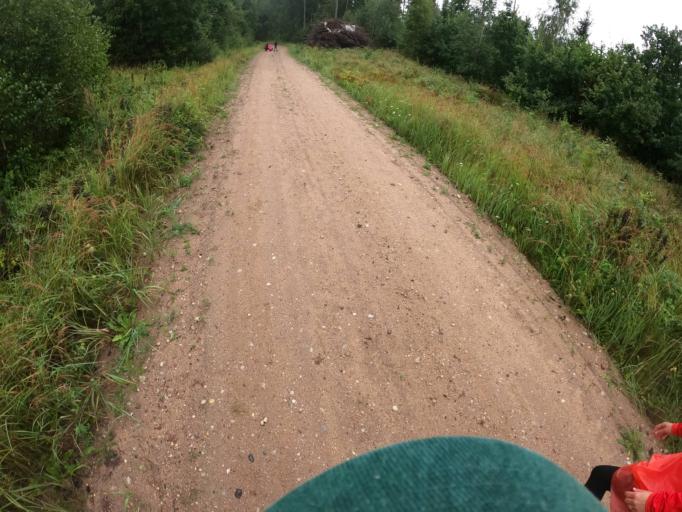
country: LV
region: Skrunda
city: Skrunda
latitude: 56.7975
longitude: 21.8434
